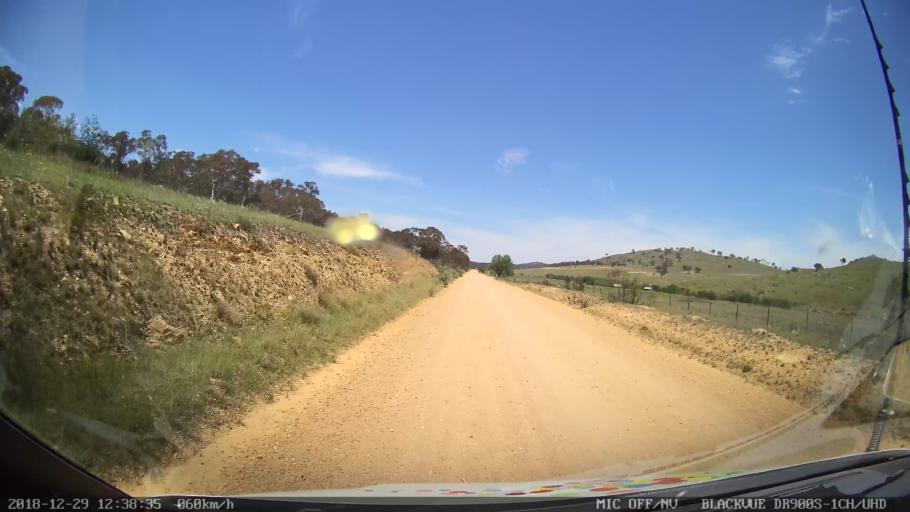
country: AU
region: Australian Capital Territory
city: Macarthur
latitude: -35.5900
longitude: 149.2289
